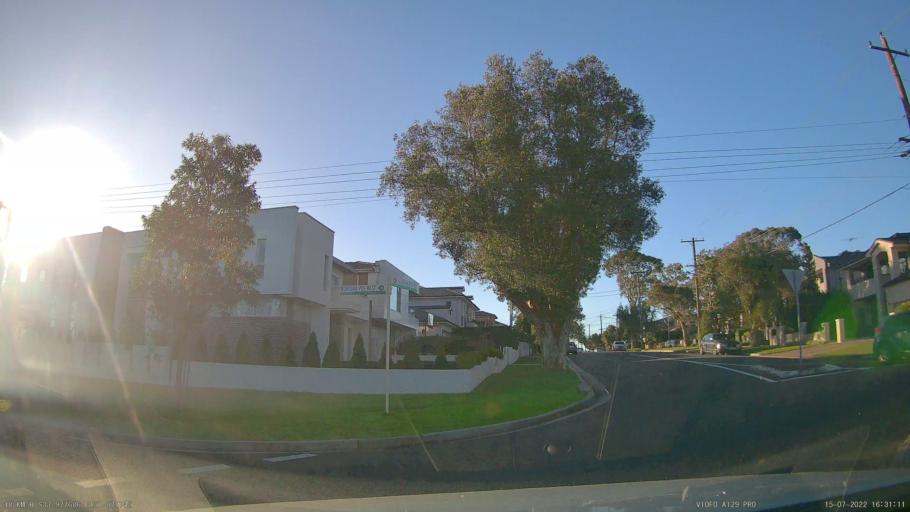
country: AU
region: New South Wales
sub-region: Hurstville
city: Oatley
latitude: -33.9775
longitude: 151.0718
